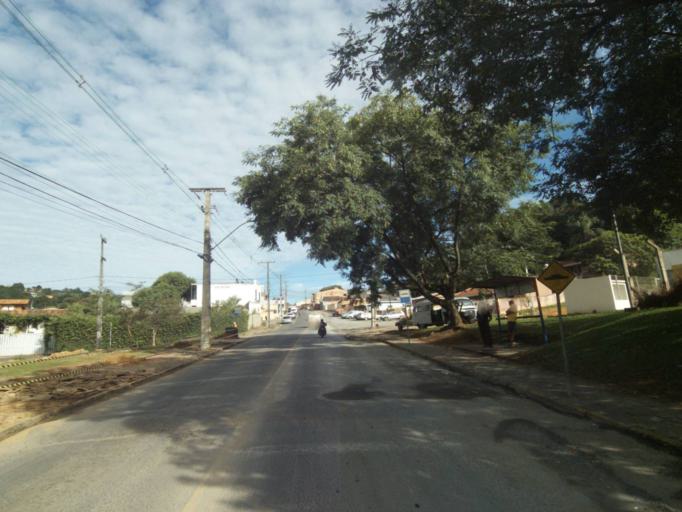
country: BR
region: Parana
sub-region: Telemaco Borba
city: Telemaco Borba
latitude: -24.3420
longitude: -50.6131
